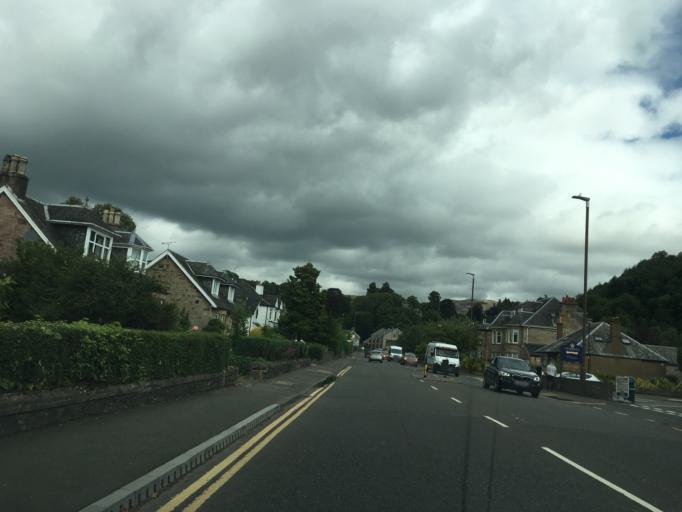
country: GB
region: Scotland
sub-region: Stirling
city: Stirling
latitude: 56.1365
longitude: -3.9260
